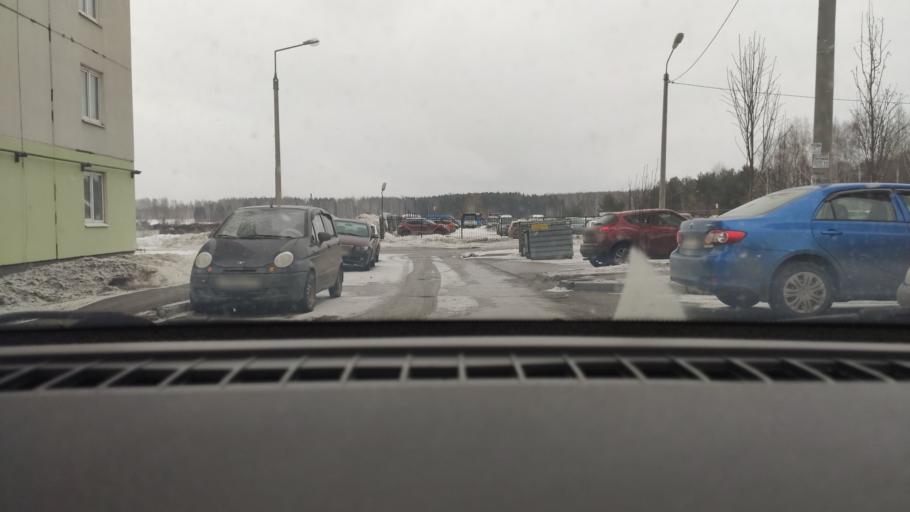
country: RU
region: Perm
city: Polazna
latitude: 58.1355
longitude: 56.4008
